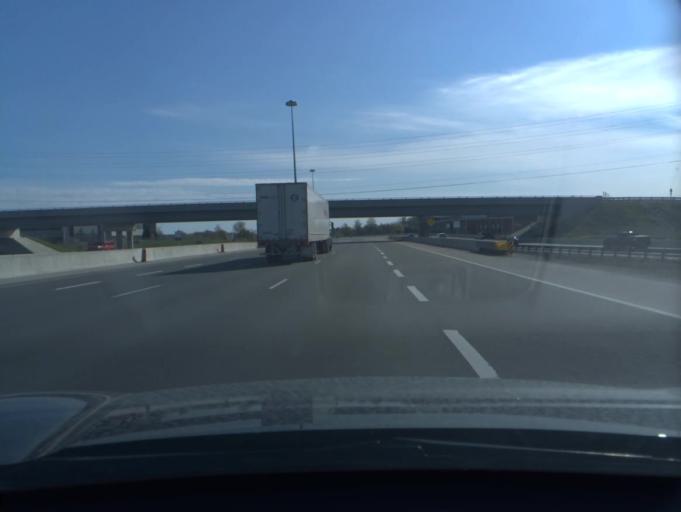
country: CA
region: Ontario
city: North Perth
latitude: 43.8095
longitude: -80.9999
